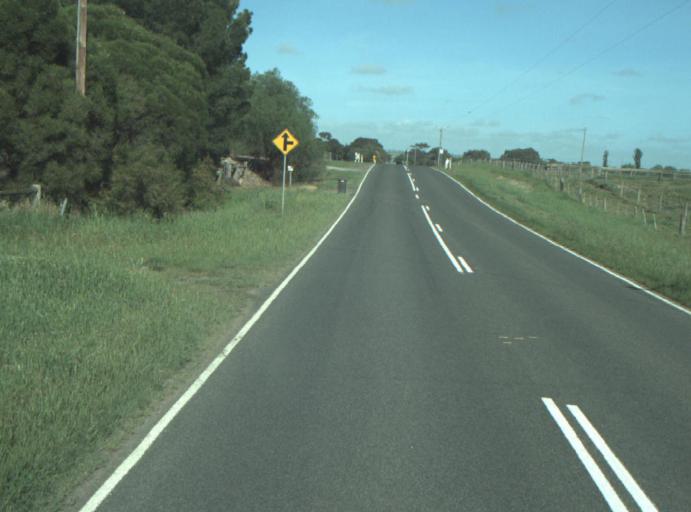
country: AU
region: Victoria
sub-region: Greater Geelong
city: Lara
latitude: -38.0080
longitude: 144.3921
